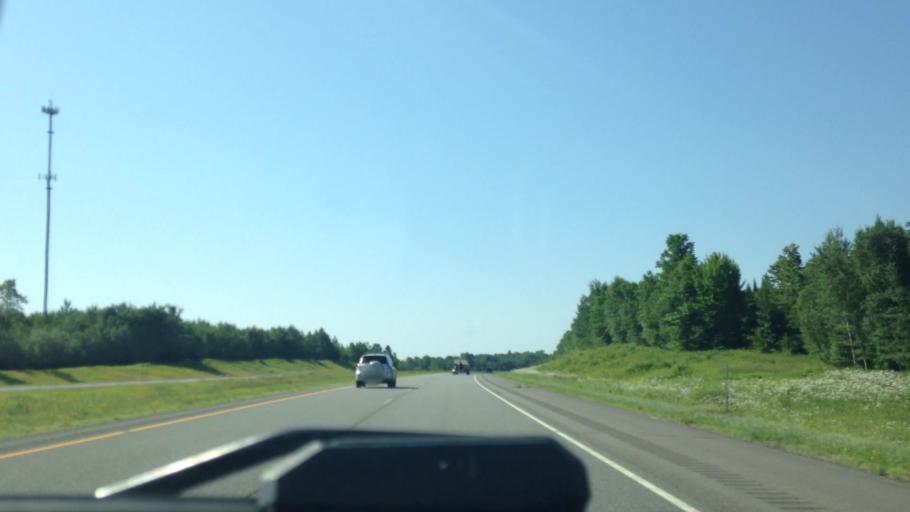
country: US
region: Wisconsin
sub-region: Douglas County
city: Lake Nebagamon
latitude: 46.4256
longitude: -91.8109
